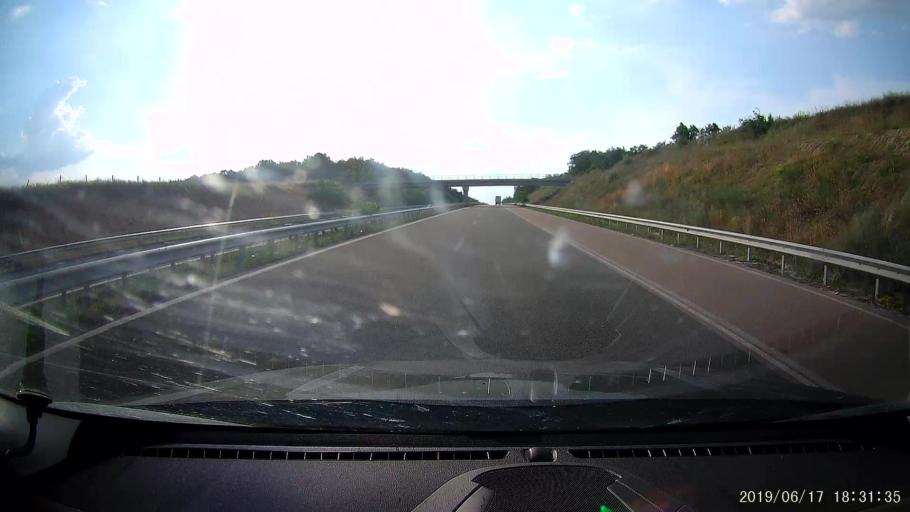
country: BG
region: Khaskovo
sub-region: Obshtina Dimitrovgrad
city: Dimitrovgrad
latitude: 42.0483
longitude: 25.5006
